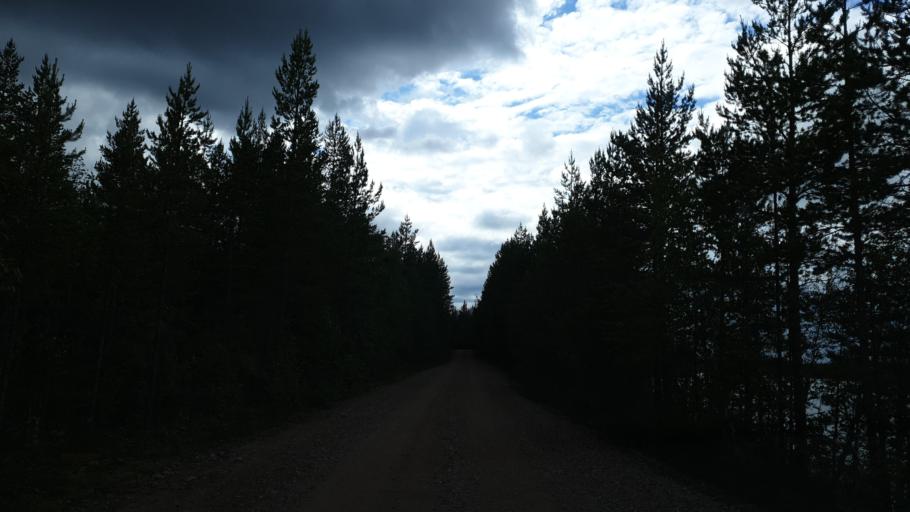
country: SE
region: Jaemtland
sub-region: Harjedalens Kommun
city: Sveg
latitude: 62.0334
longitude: 14.4908
